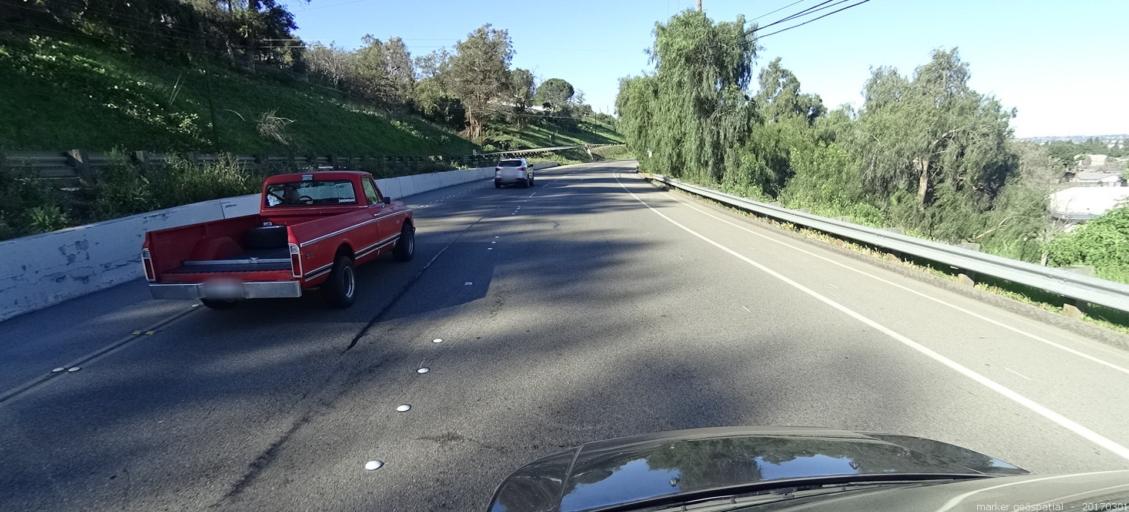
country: US
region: California
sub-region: Orange County
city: Villa Park
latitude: 33.8505
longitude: -117.8069
